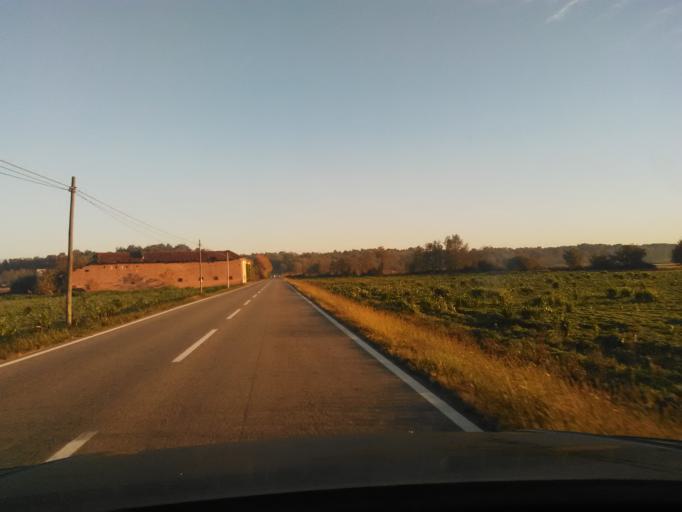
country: IT
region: Piedmont
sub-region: Provincia di Vercelli
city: Carisio
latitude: 45.3941
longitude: 8.1855
